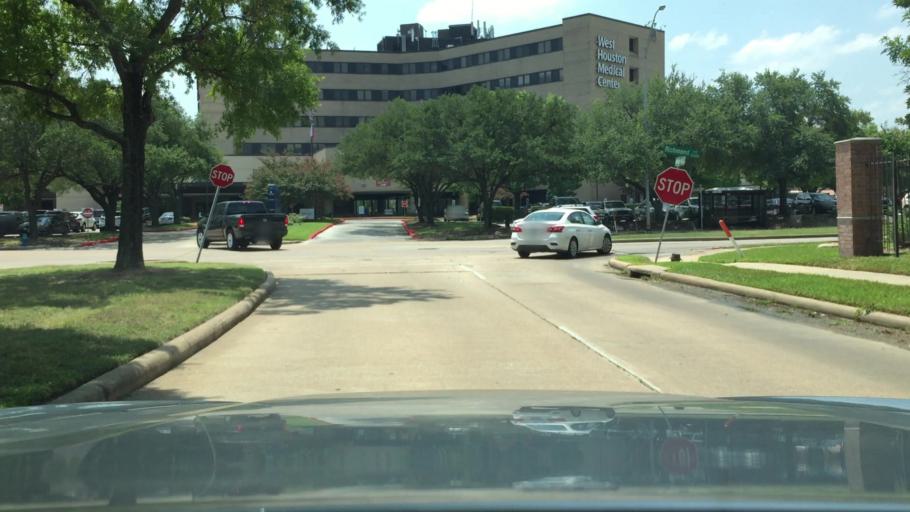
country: US
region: Texas
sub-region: Harris County
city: Bunker Hill Village
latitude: 29.7307
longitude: -95.5952
